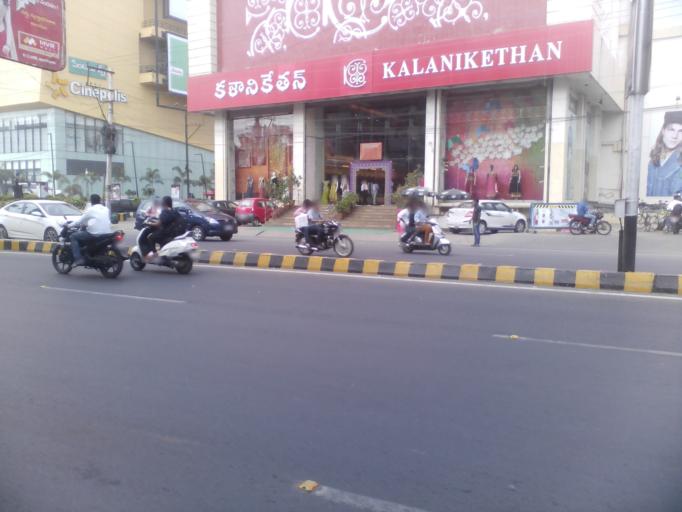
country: IN
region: Andhra Pradesh
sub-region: Krishna
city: Vijayawada
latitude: 16.5019
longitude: 80.6432
